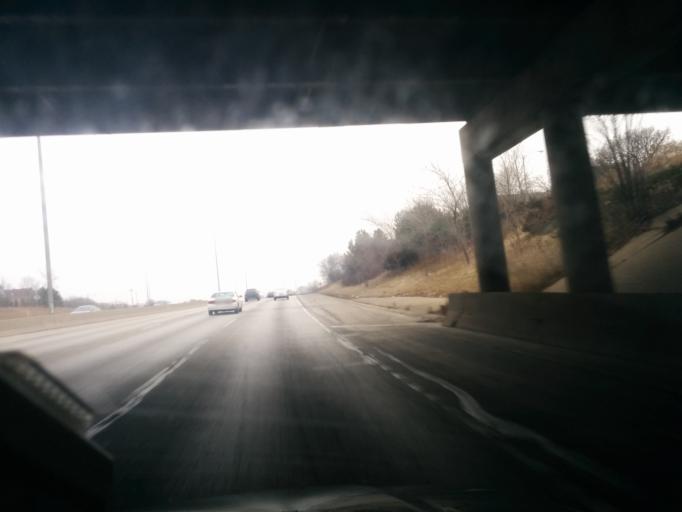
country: US
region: Wisconsin
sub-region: Milwaukee County
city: Shorewood
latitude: 43.0817
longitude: -87.9207
